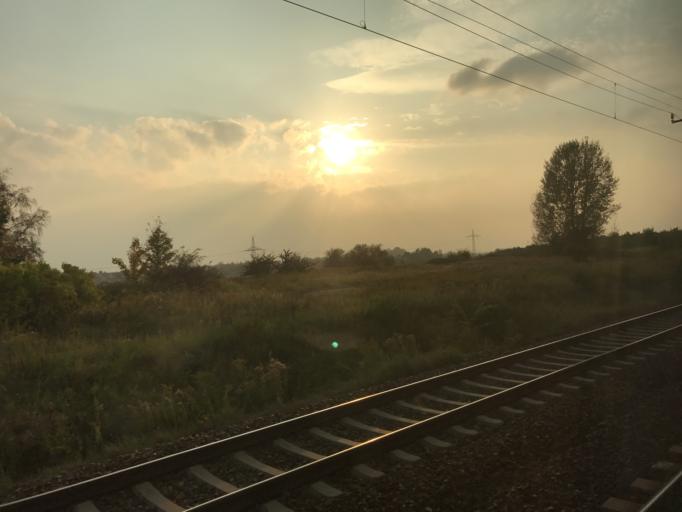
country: DE
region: Saxony
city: Schkeuditz
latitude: 51.3928
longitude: 12.2847
